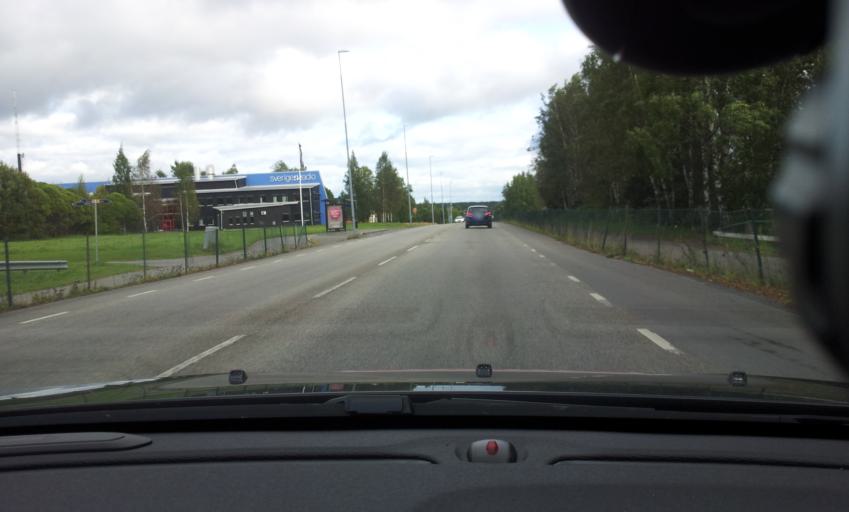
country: SE
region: Jaemtland
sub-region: OEstersunds Kommun
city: Ostersund
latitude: 63.1536
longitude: 14.6891
